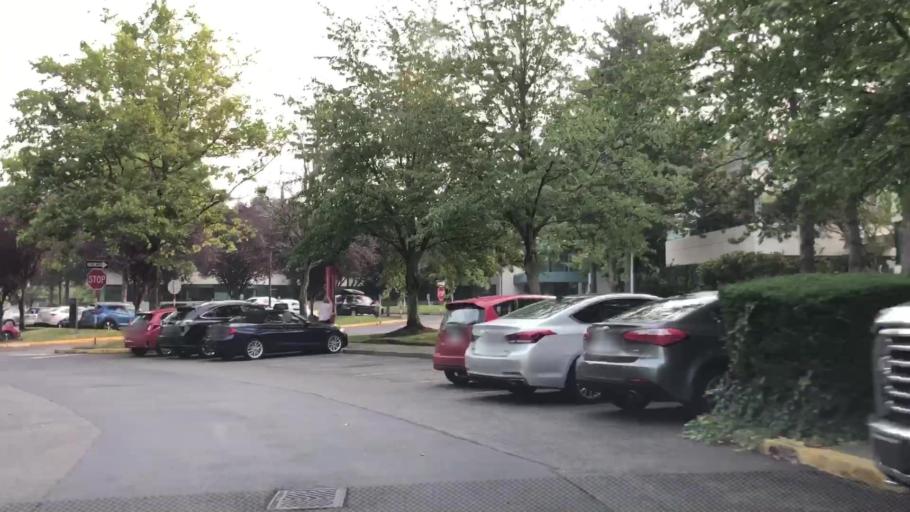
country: US
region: Washington
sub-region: King County
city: Redmond
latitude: 47.6402
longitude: -122.1290
